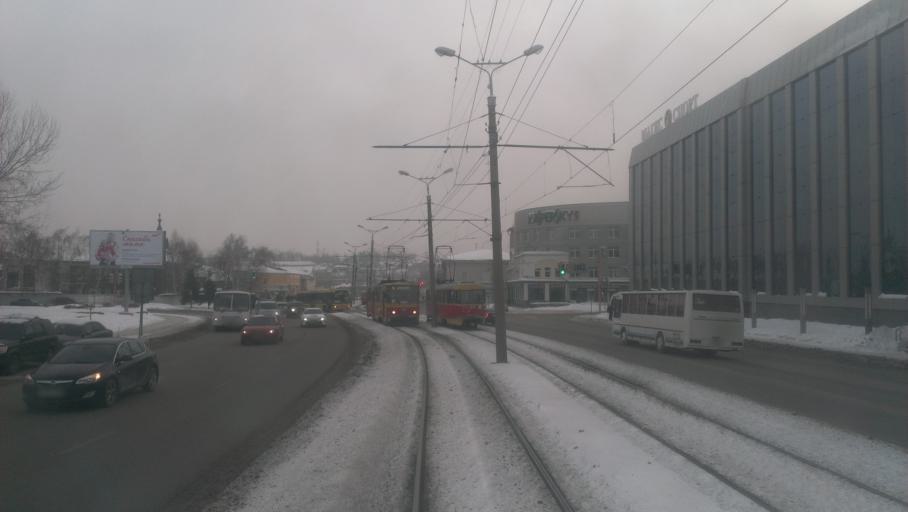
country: RU
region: Altai Krai
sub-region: Gorod Barnaulskiy
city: Barnaul
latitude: 53.3311
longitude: 83.7820
